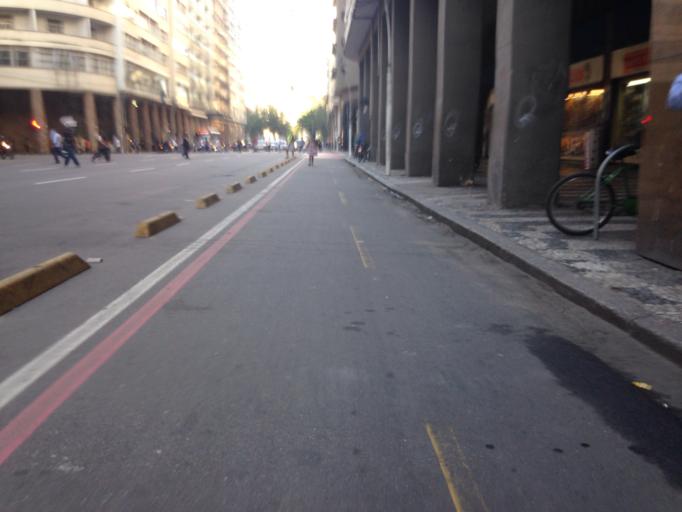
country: BR
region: Rio de Janeiro
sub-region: Niteroi
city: Niteroi
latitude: -22.8935
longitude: -43.1204
